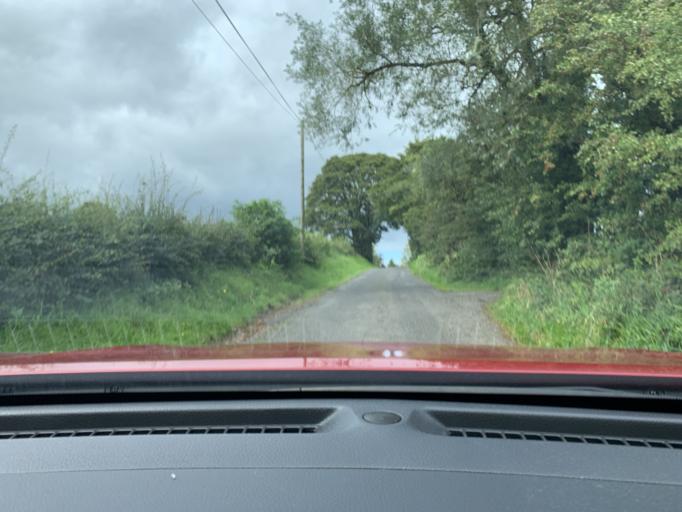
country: IE
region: Connaught
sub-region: Sligo
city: Collooney
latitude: 54.1541
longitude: -8.4270
